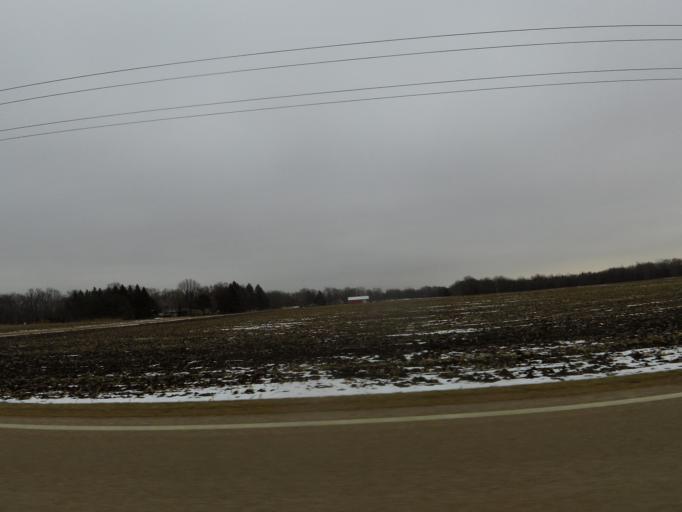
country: US
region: Minnesota
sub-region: Carver County
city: Carver
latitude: 44.7503
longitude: -93.6840
